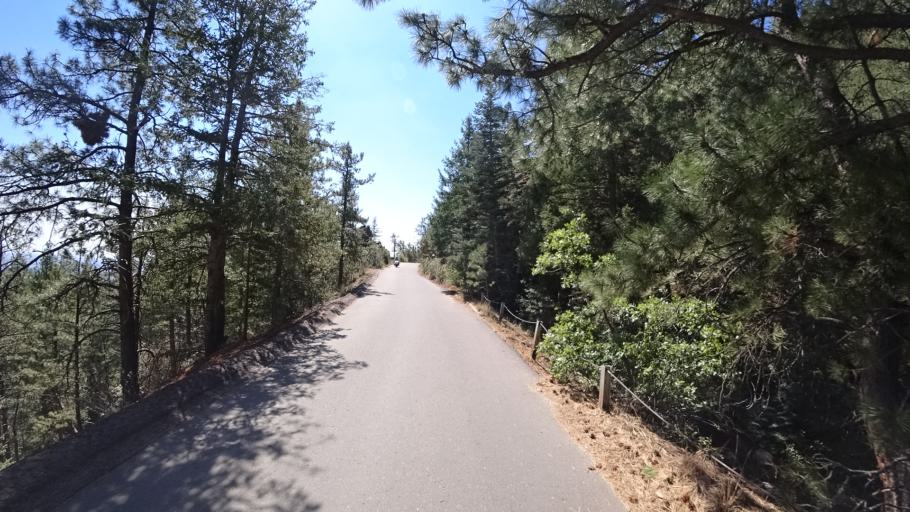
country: US
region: Colorado
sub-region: El Paso County
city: Colorado Springs
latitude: 38.7998
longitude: -104.8767
